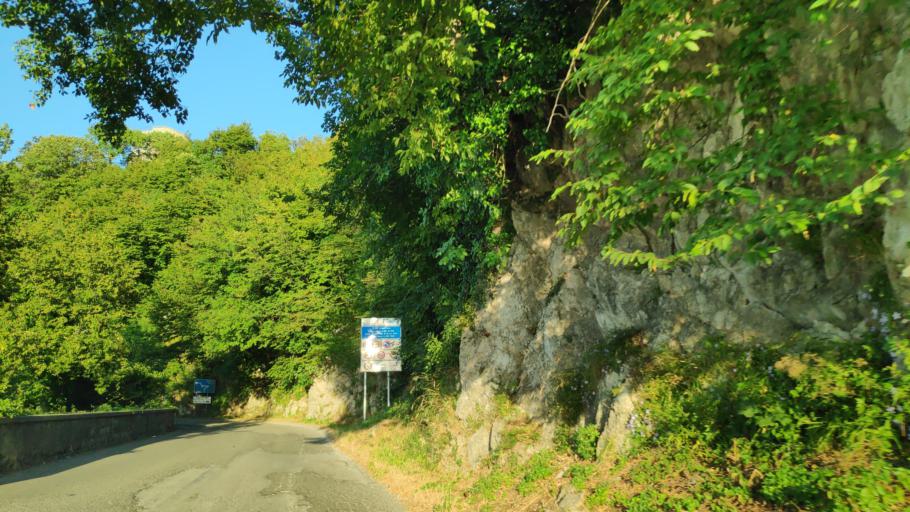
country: IT
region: Campania
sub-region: Provincia di Salerno
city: Pietre
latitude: 40.7183
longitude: 14.6171
